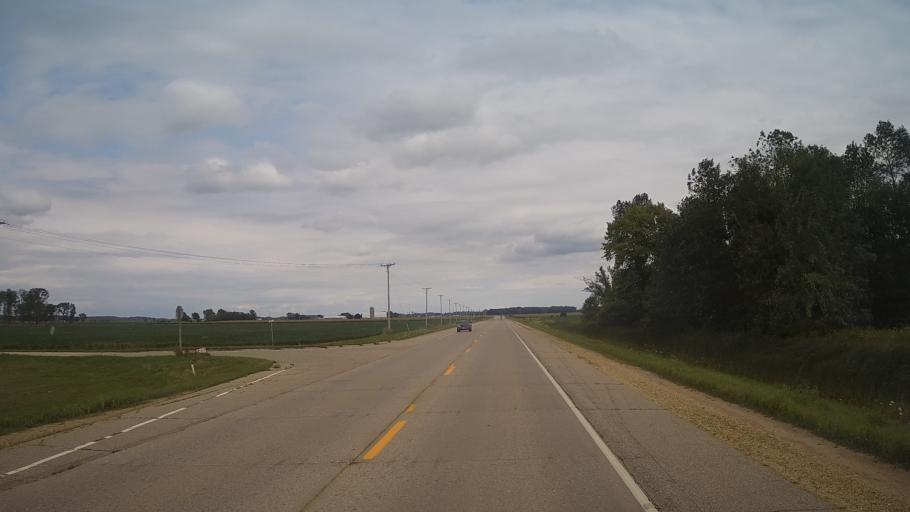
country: US
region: Wisconsin
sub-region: Waushara County
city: Redgranite
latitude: 44.0375
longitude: -89.0622
